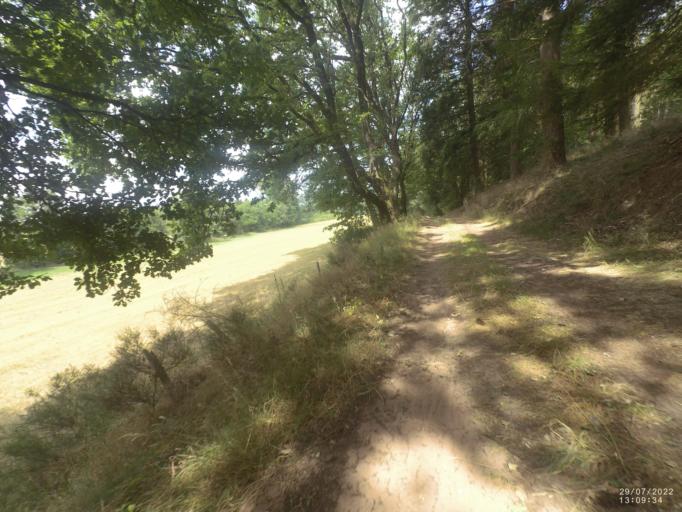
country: DE
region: Rheinland-Pfalz
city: Duppach
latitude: 50.2706
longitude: 6.5804
